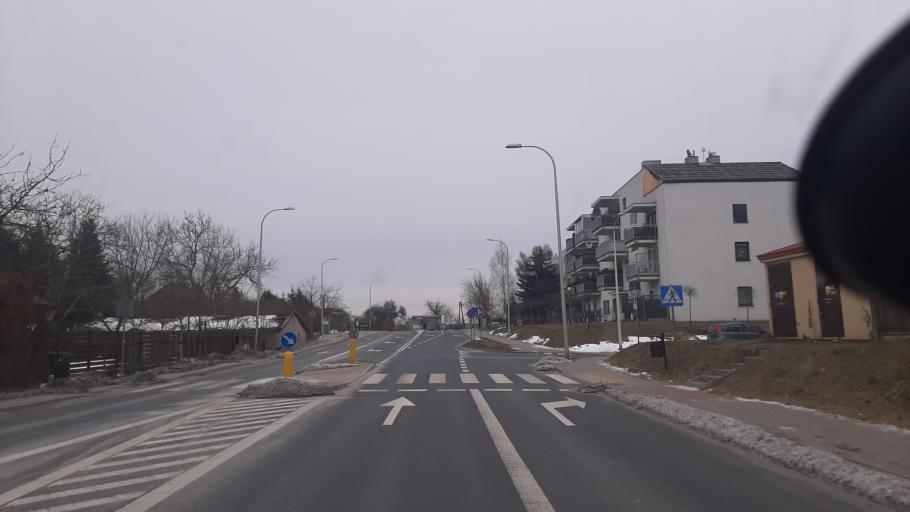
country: PL
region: Lublin Voivodeship
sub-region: Powiat lubelski
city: Lublin
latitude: 51.2764
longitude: 22.5805
